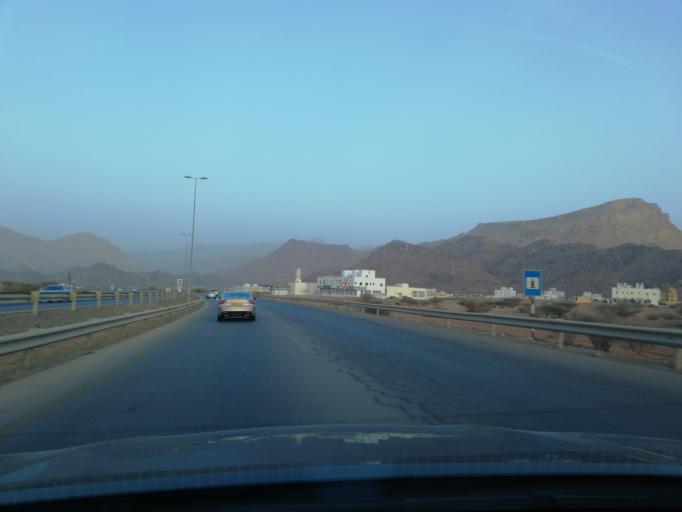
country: OM
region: Muhafazat ad Dakhiliyah
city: Bidbid
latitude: 23.4588
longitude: 58.1694
